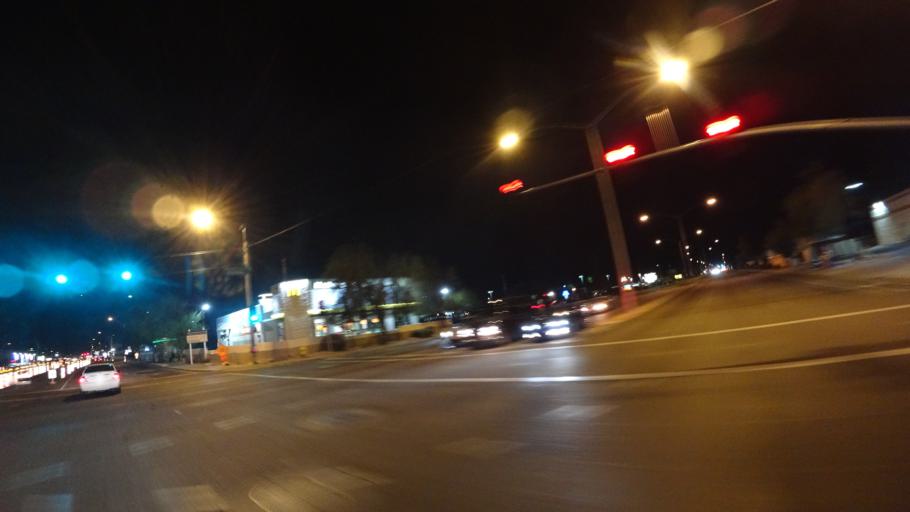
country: US
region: Arizona
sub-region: Maricopa County
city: Mesa
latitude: 33.4155
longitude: -111.7882
